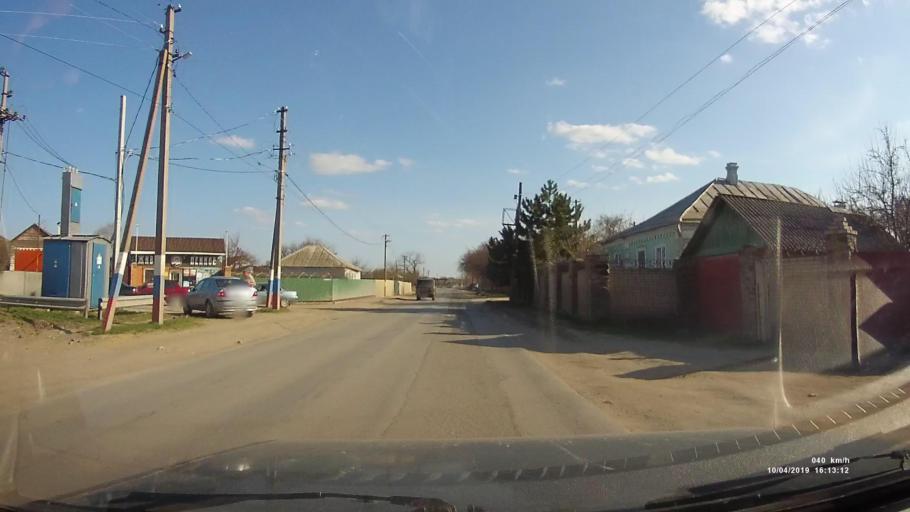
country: RU
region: Rostov
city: Staraya Stanitsa
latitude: 48.3444
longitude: 40.2877
